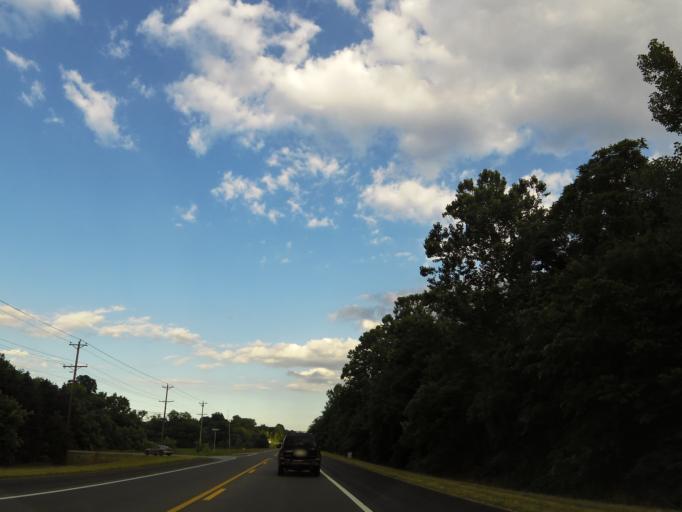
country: US
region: Tennessee
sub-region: Maury County
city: Columbia
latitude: 35.6354
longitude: -86.9601
